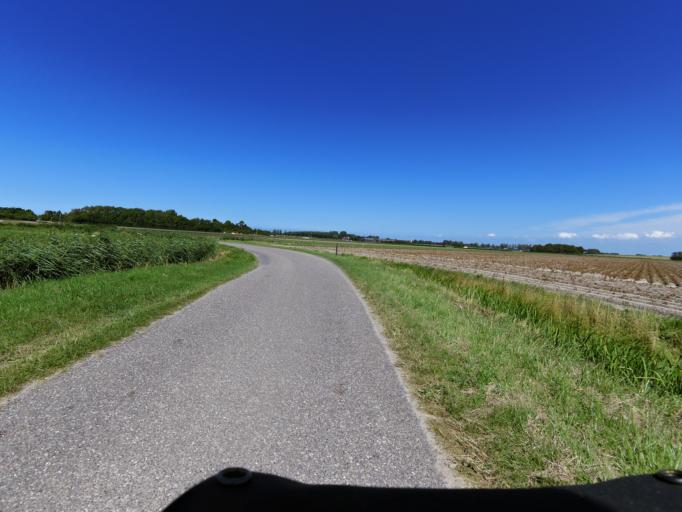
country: NL
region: South Holland
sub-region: Gemeente Goeree-Overflakkee
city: Goedereede
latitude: 51.8118
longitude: 3.9848
